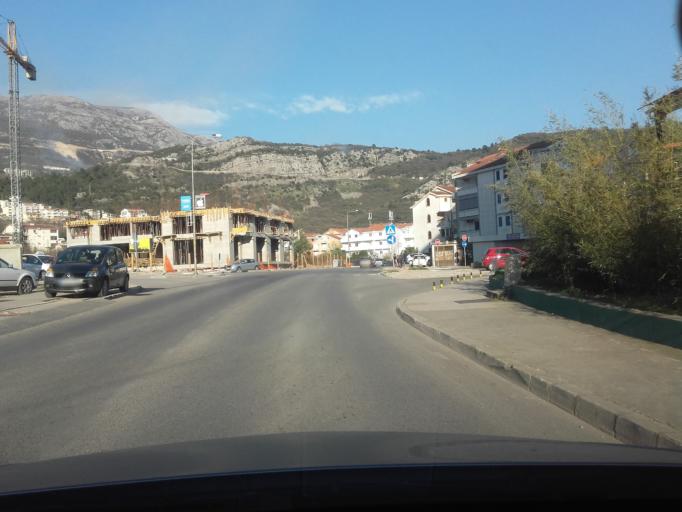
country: ME
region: Budva
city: Budva
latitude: 42.2945
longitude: 18.8408
